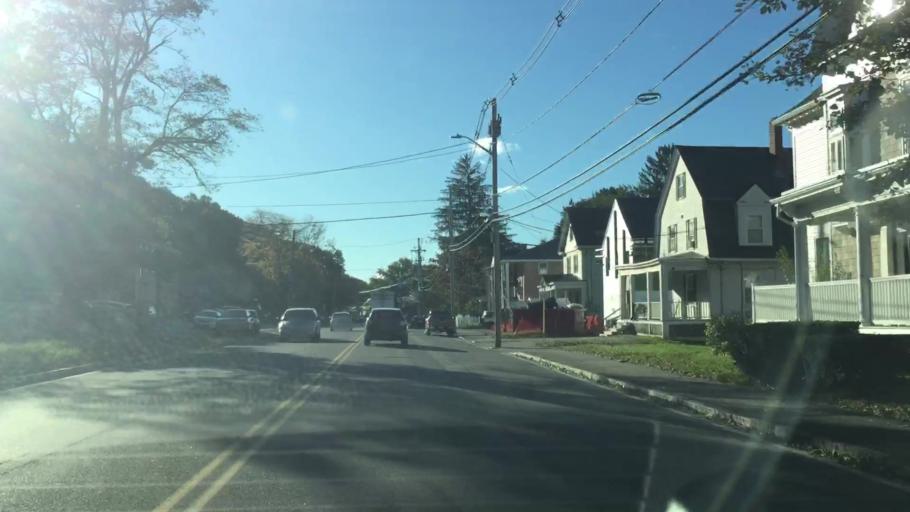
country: US
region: Massachusetts
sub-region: Middlesex County
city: Lowell
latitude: 42.6392
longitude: -71.2955
